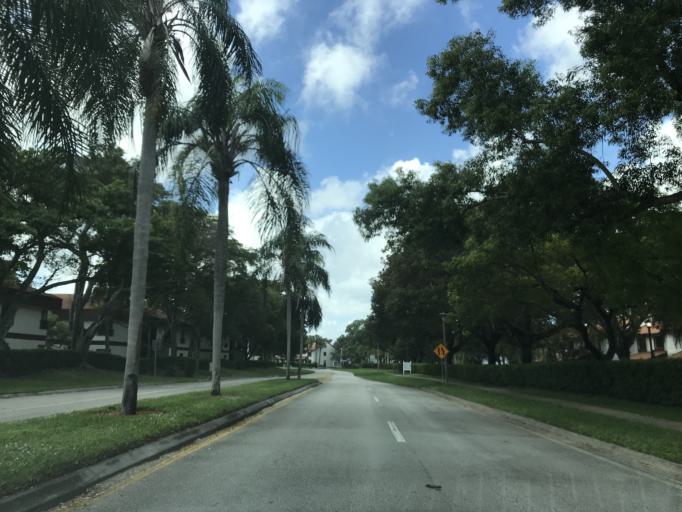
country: US
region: Florida
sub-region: Broward County
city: Coconut Creek
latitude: 26.2722
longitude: -80.1868
